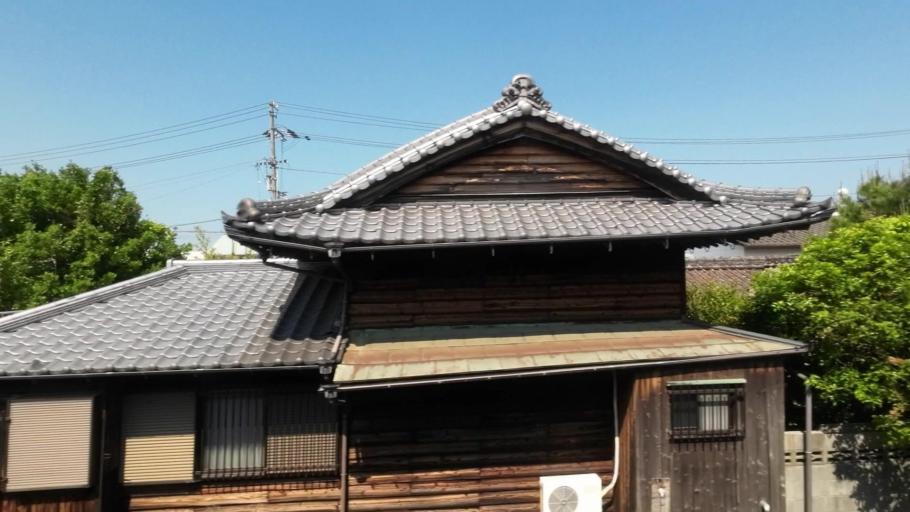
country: JP
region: Ehime
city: Kawanoecho
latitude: 34.0187
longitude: 133.5770
